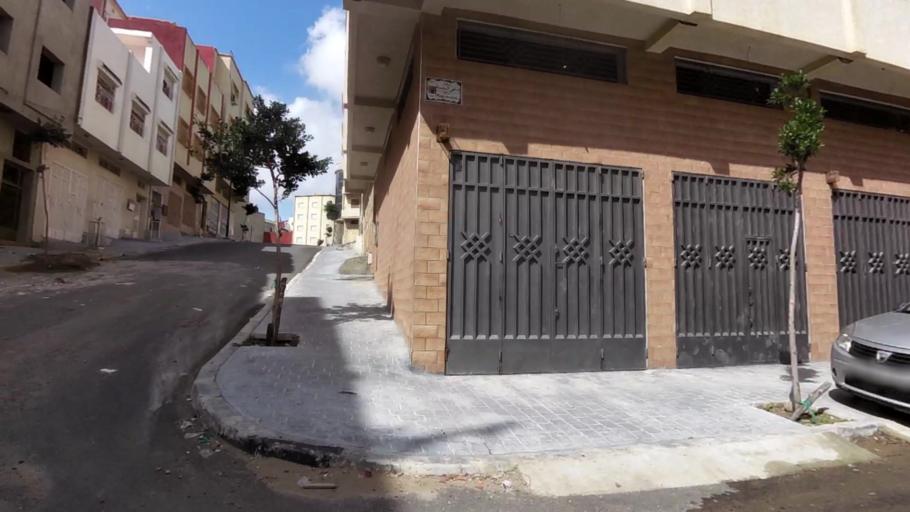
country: MA
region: Tanger-Tetouan
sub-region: Tanger-Assilah
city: Tangier
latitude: 35.7678
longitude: -5.7619
